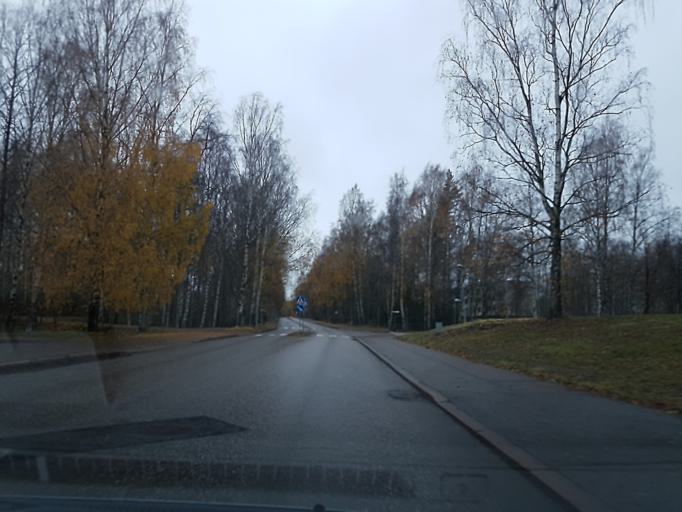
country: FI
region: Uusimaa
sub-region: Helsinki
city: Vantaa
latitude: 60.2303
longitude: 25.0873
